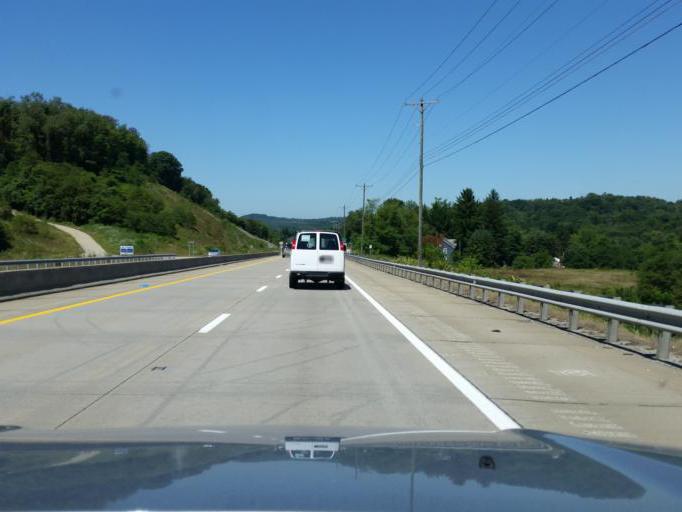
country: US
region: Pennsylvania
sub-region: Westmoreland County
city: Murrysville
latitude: 40.4156
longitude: -79.6421
